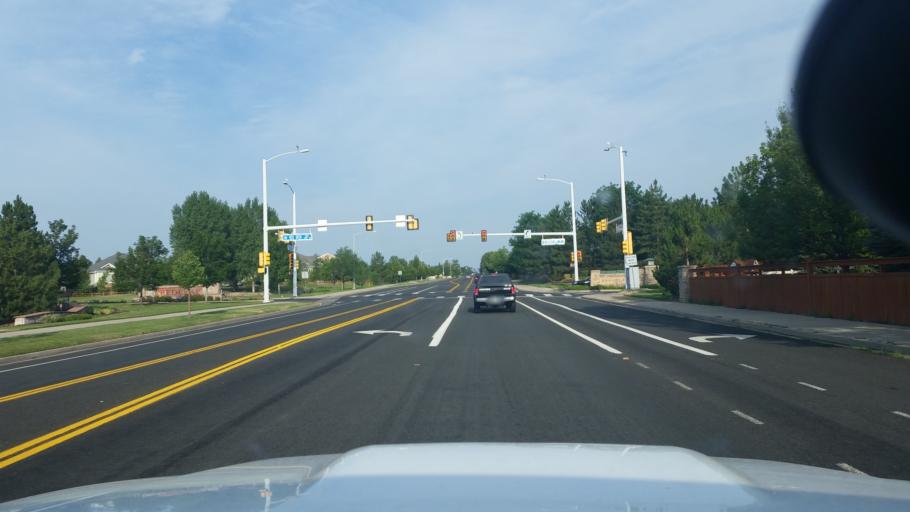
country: US
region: Colorado
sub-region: Broomfield County
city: Broomfield
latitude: 39.9433
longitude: -105.0449
